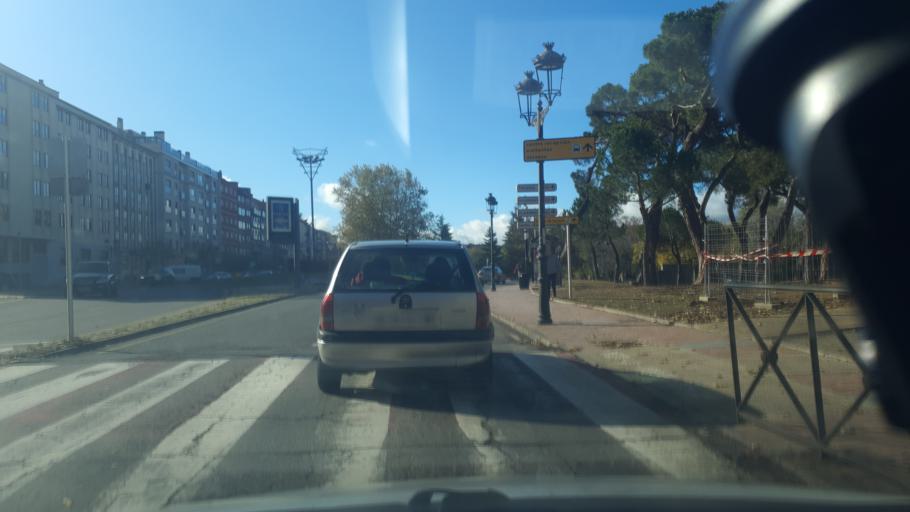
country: ES
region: Castille and Leon
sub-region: Provincia de Avila
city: Avila
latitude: 40.6585
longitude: -4.6836
